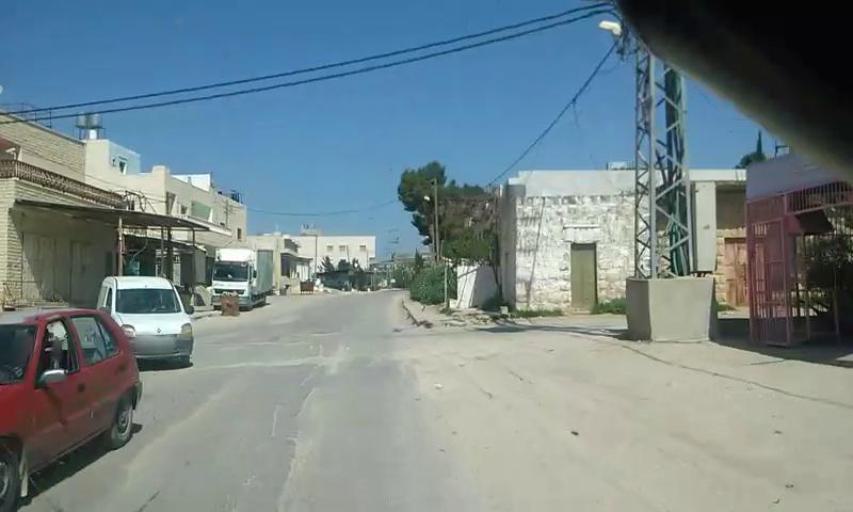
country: PS
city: Dayr Samit
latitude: 31.5203
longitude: 34.9768
